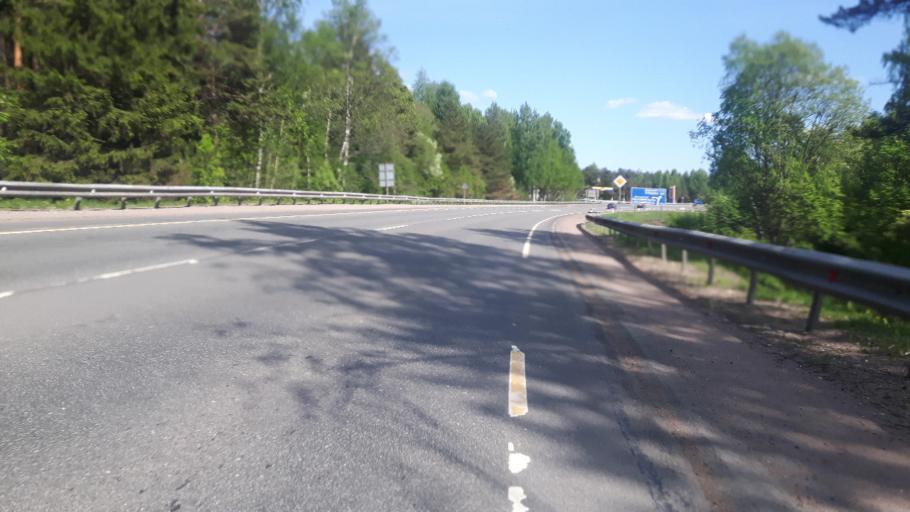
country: RU
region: Leningrad
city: Vyborg
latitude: 60.7449
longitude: 28.6708
